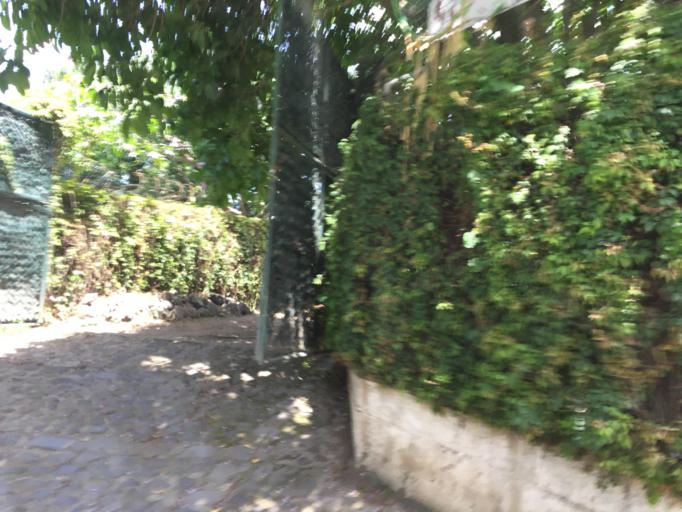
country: GT
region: Sacatepequez
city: Ciudad Vieja
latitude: 14.5287
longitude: -90.7433
